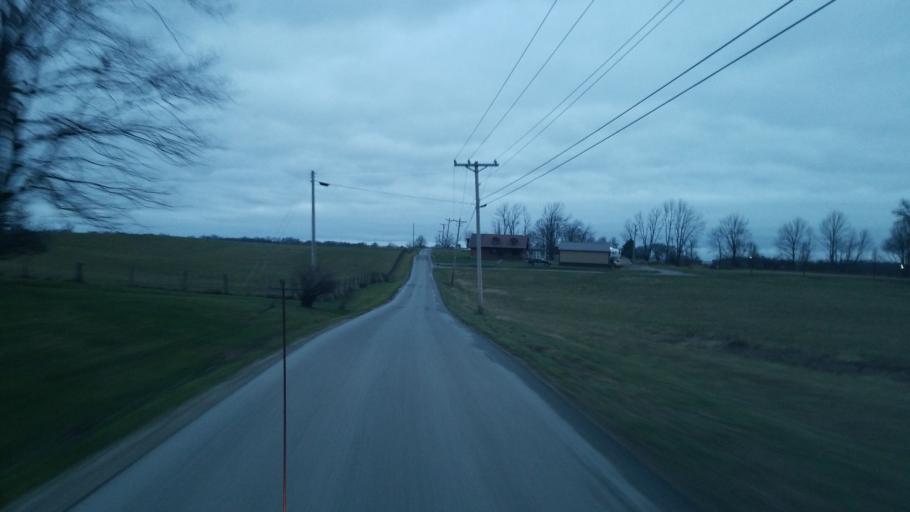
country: US
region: Kentucky
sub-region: Fleming County
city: Flemingsburg
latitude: 38.4885
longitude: -83.6564
